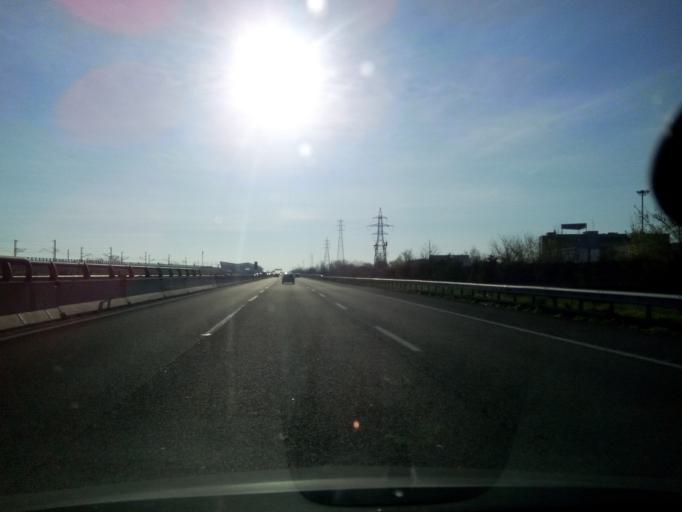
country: IT
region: Emilia-Romagna
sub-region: Provincia di Reggio Emilia
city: Reggio nell'Emilia
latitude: 44.7265
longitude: 10.6407
